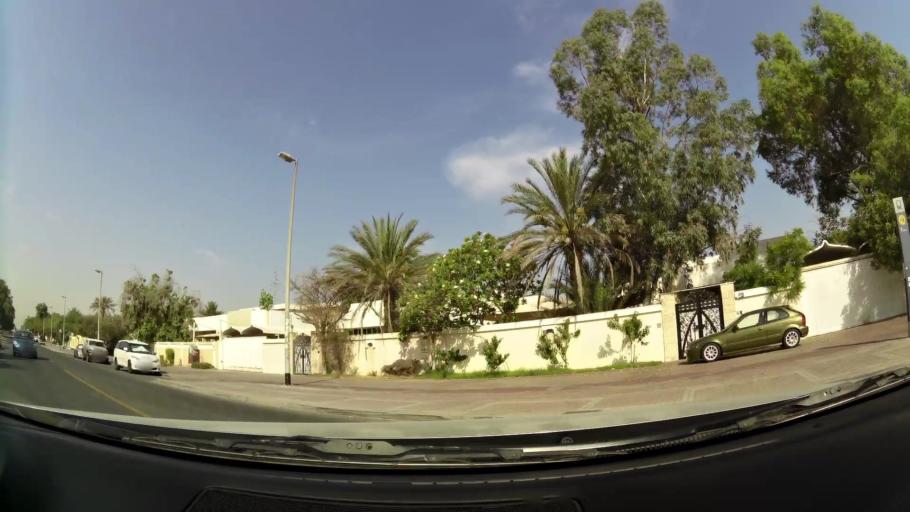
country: AE
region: Ash Shariqah
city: Sharjah
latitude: 25.2274
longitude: 55.3911
